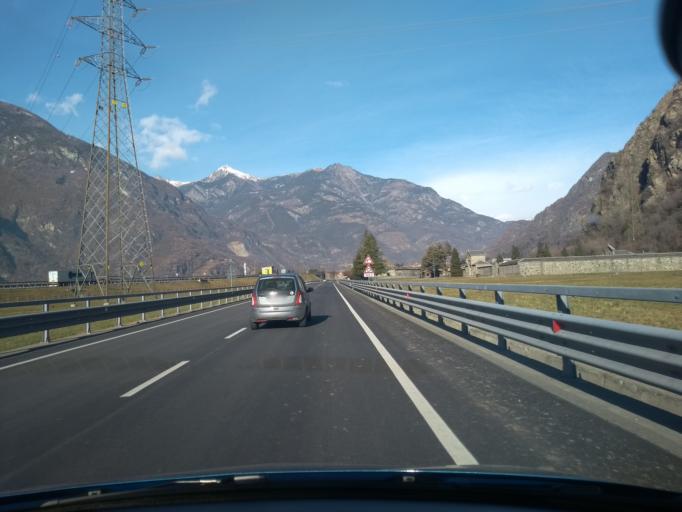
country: IT
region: Aosta Valley
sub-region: Valle d'Aosta
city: Issogne
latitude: 45.6562
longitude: 7.6976
